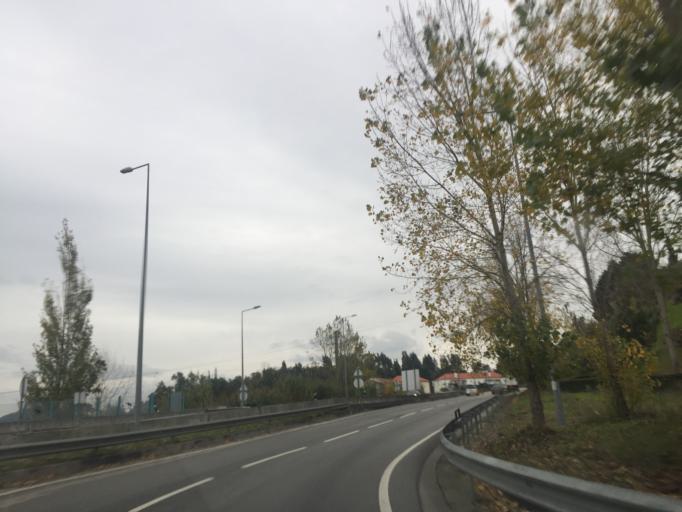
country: PT
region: Coimbra
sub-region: Coimbra
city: Coimbra
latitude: 40.1909
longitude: -8.4312
